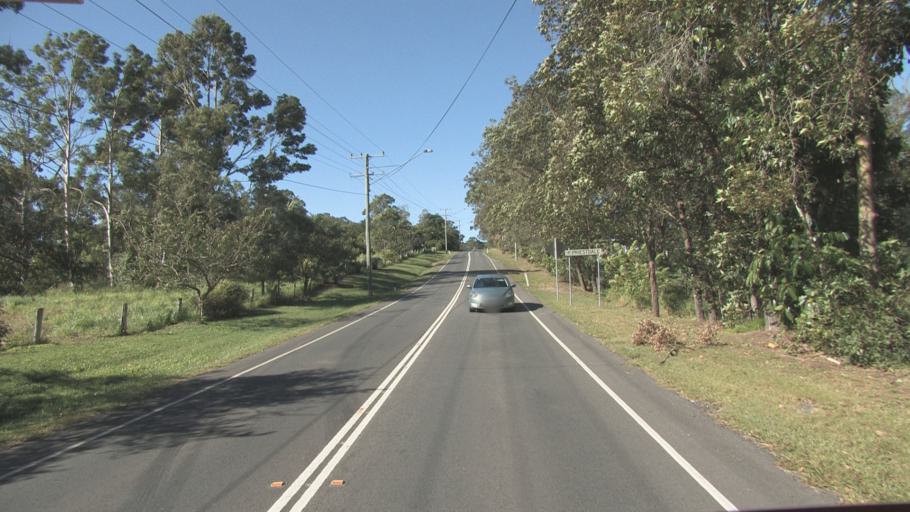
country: AU
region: Queensland
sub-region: Logan
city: Rochedale South
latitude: -27.5911
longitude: 153.1438
